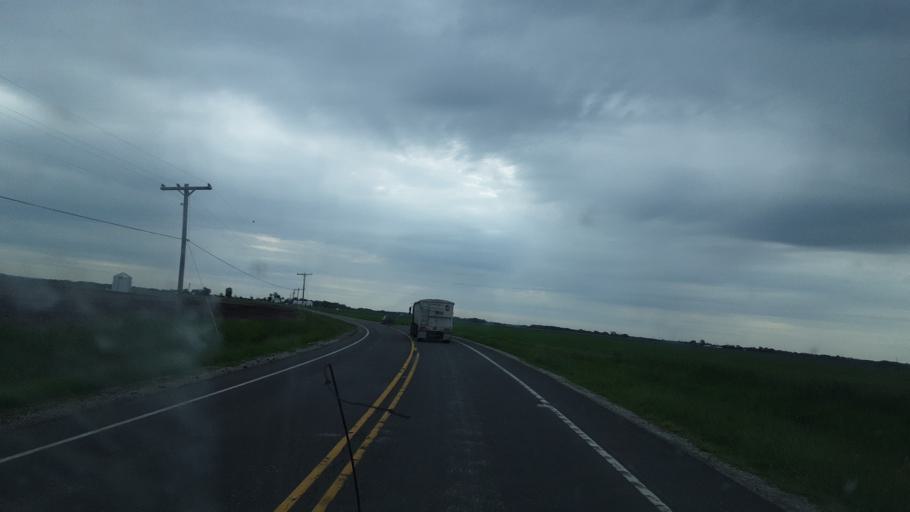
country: US
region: Illinois
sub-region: Fulton County
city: Lewistown
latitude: 40.3423
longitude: -90.2658
